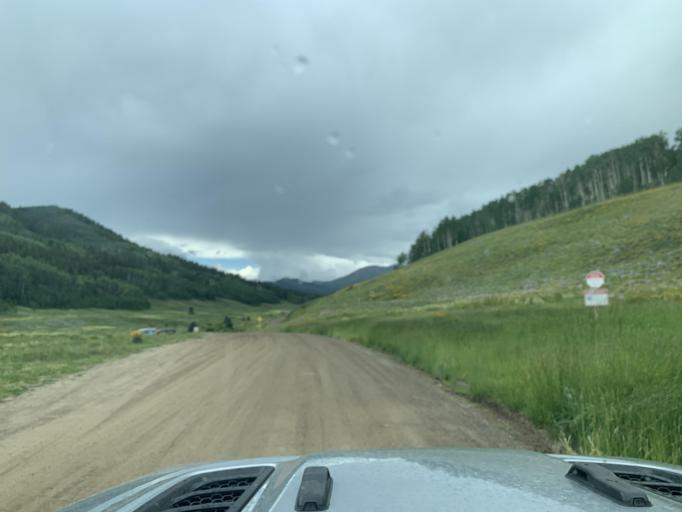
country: US
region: Colorado
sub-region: Gunnison County
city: Crested Butte
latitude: 38.9147
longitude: -107.0005
